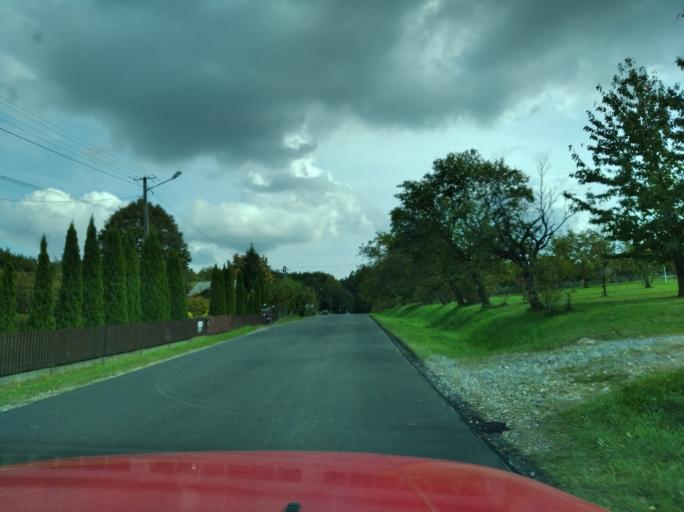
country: PL
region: Subcarpathian Voivodeship
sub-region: Powiat rzeszowski
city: Straszydle
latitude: 49.9338
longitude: 21.9856
